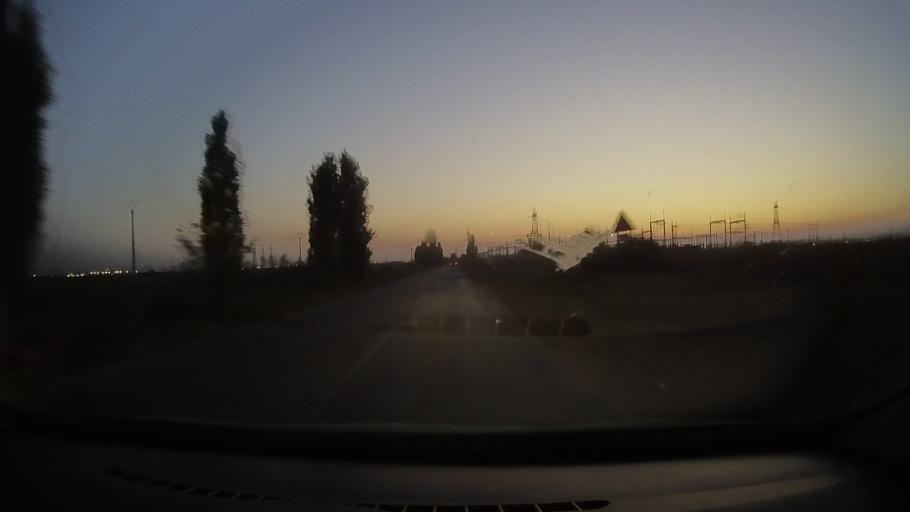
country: RO
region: Arad
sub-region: Comuna Vladimirescu
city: Vladimirescu
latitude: 46.1853
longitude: 21.3846
